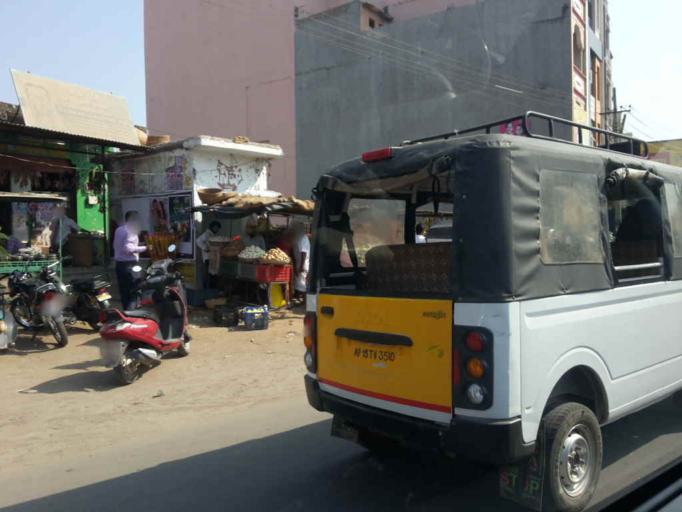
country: IN
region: Telangana
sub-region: Karimnagar
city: Koratla
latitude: 18.8480
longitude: 78.6220
